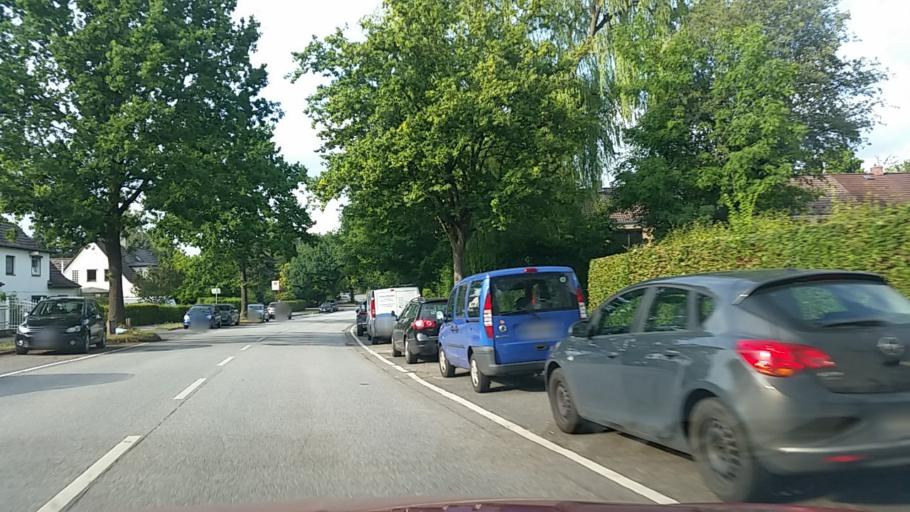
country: DE
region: Hamburg
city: Harburg
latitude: 53.4410
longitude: 9.9680
